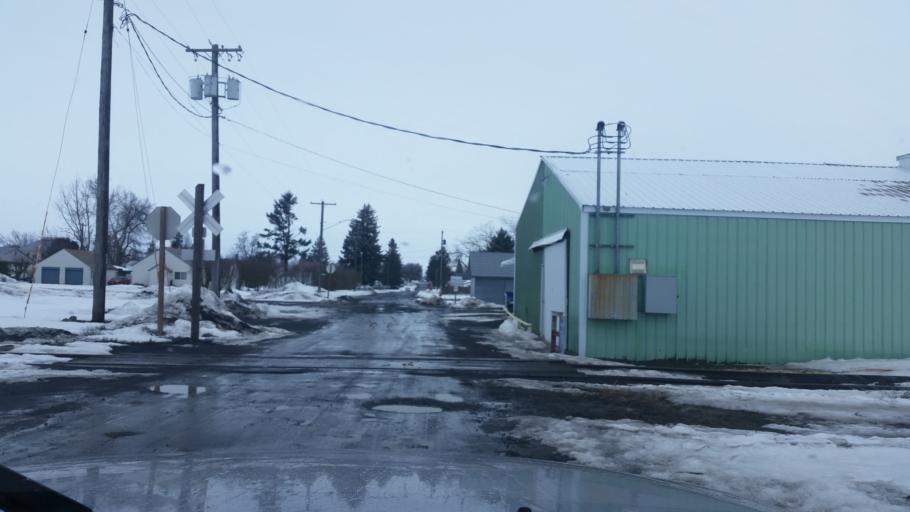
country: US
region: Washington
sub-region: Lincoln County
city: Davenport
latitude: 47.6468
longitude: -118.1472
